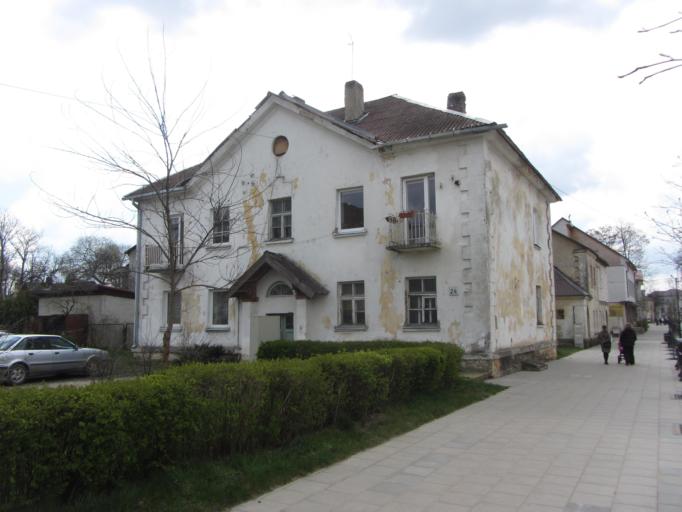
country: LT
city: Lentvaris
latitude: 54.6432
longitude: 25.0477
